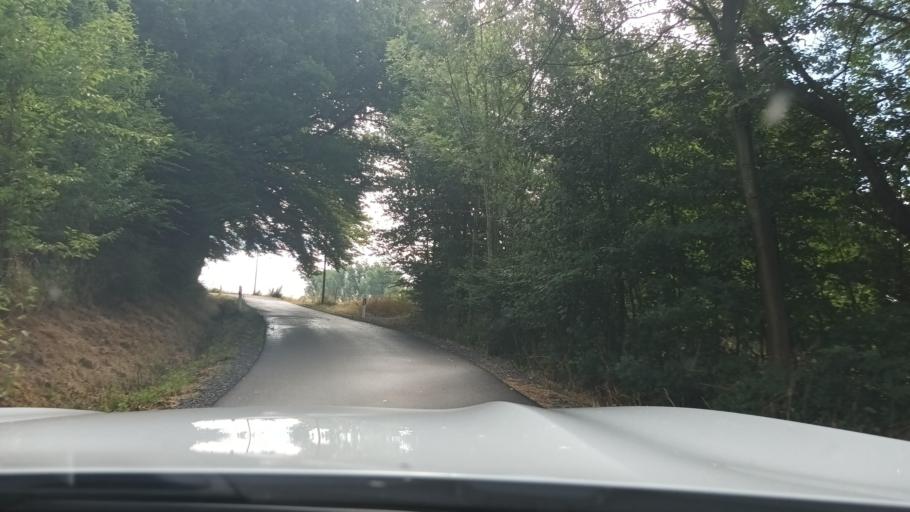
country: DE
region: North Rhine-Westphalia
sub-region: Regierungsbezirk Koln
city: Hennef
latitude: 50.7371
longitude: 7.3218
